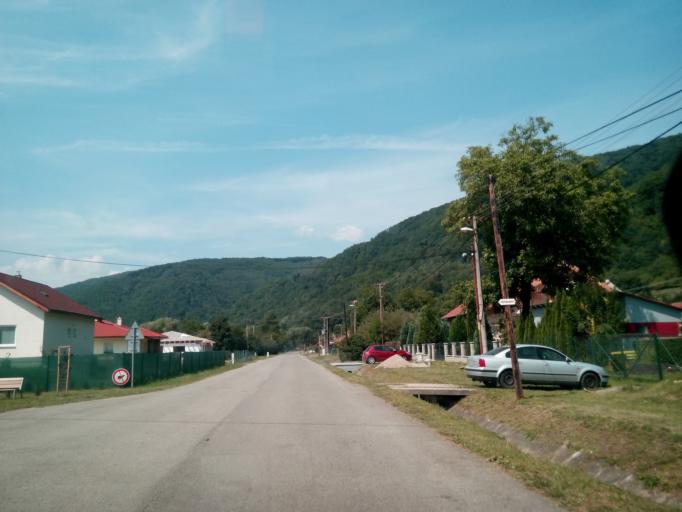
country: SK
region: Presovsky
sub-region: Okres Presov
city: Presov
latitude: 48.8781
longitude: 21.1324
